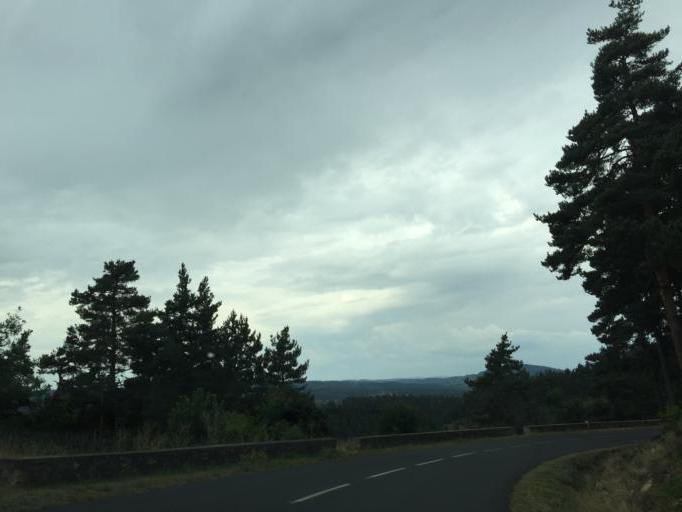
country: FR
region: Languedoc-Roussillon
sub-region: Departement de la Lozere
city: Langogne
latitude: 44.8195
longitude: 3.7794
